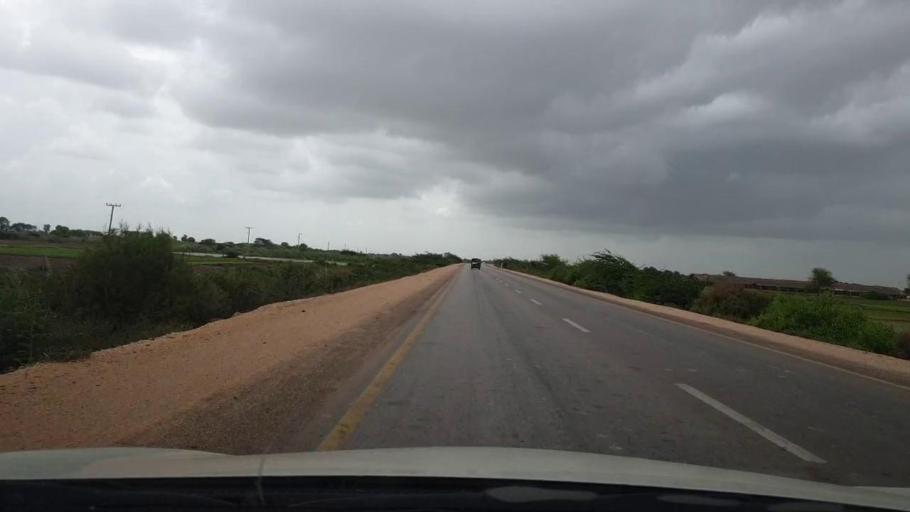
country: PK
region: Sindh
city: Mirpur Batoro
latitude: 24.6437
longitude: 68.4337
